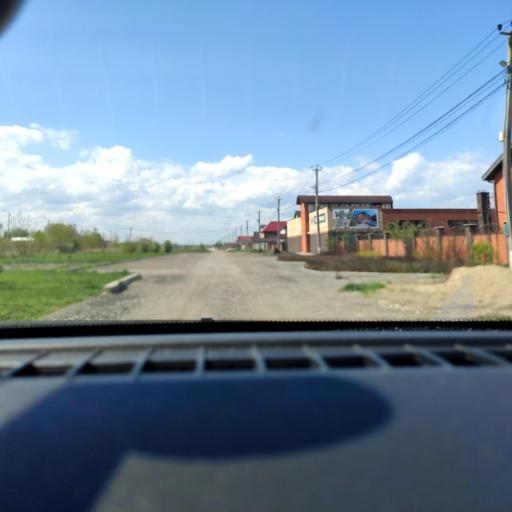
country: RU
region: Samara
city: Podstepki
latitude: 53.5230
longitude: 49.1631
